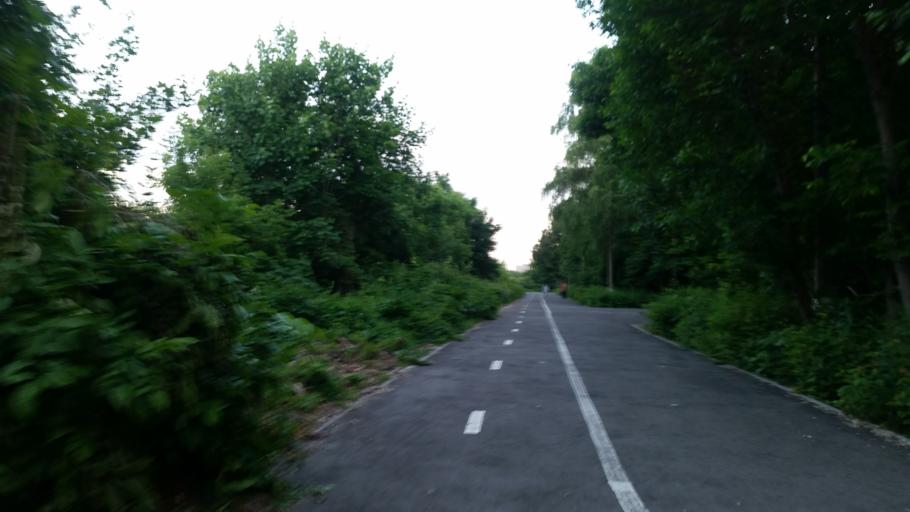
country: RU
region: Ulyanovsk
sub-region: Ulyanovskiy Rayon
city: Ulyanovsk
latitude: 54.3331
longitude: 48.4071
